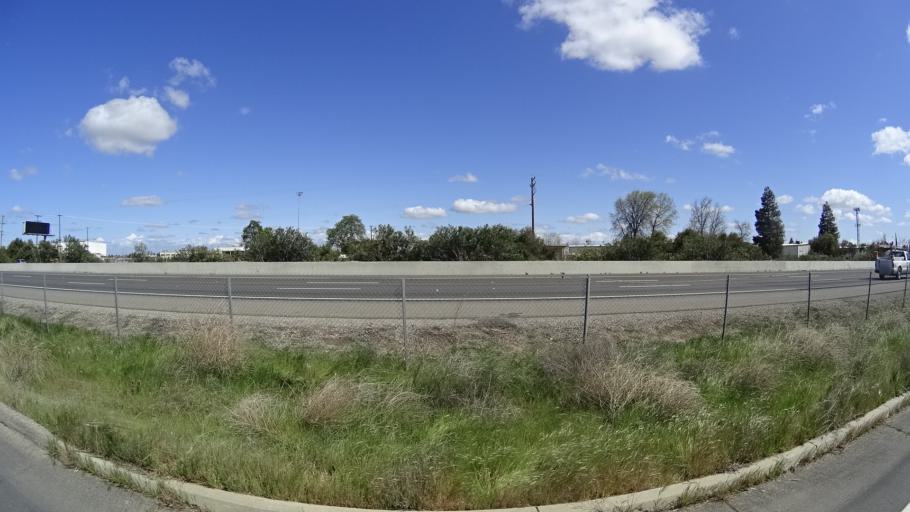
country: US
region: California
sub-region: Fresno County
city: West Park
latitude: 36.8144
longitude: -119.8957
